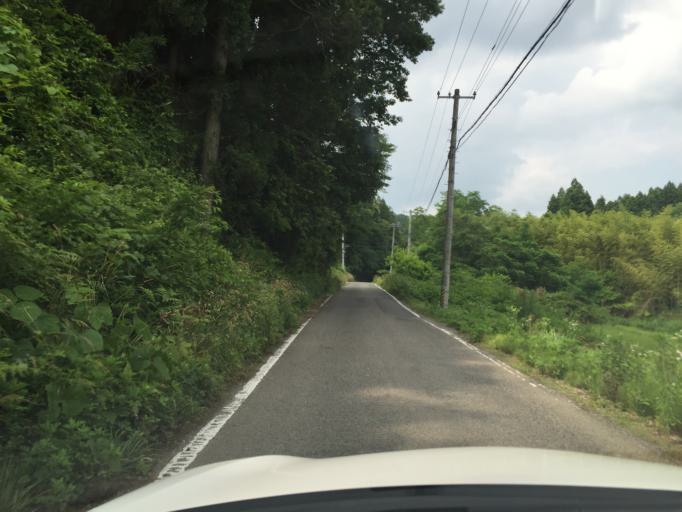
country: JP
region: Fukushima
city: Sukagawa
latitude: 37.3227
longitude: 140.4605
